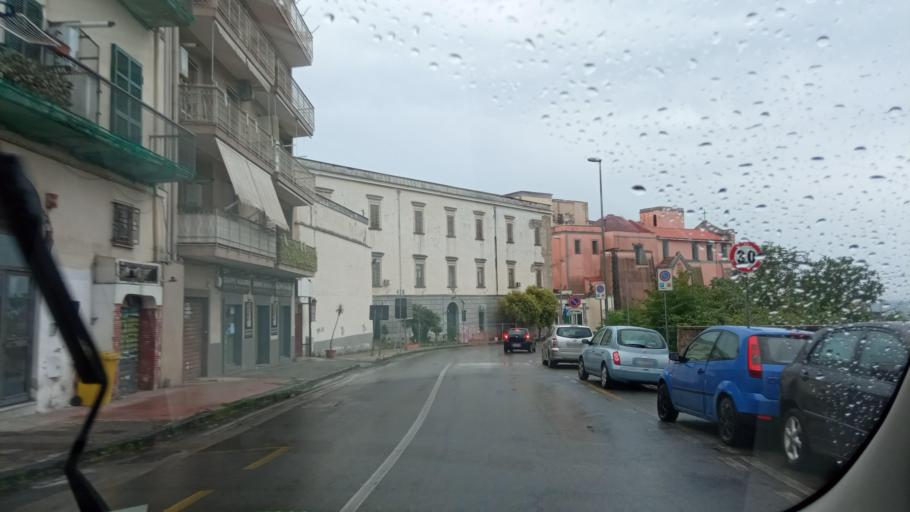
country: IT
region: Campania
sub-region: Provincia di Napoli
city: Pozzuoli
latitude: 40.8297
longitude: 14.1203
